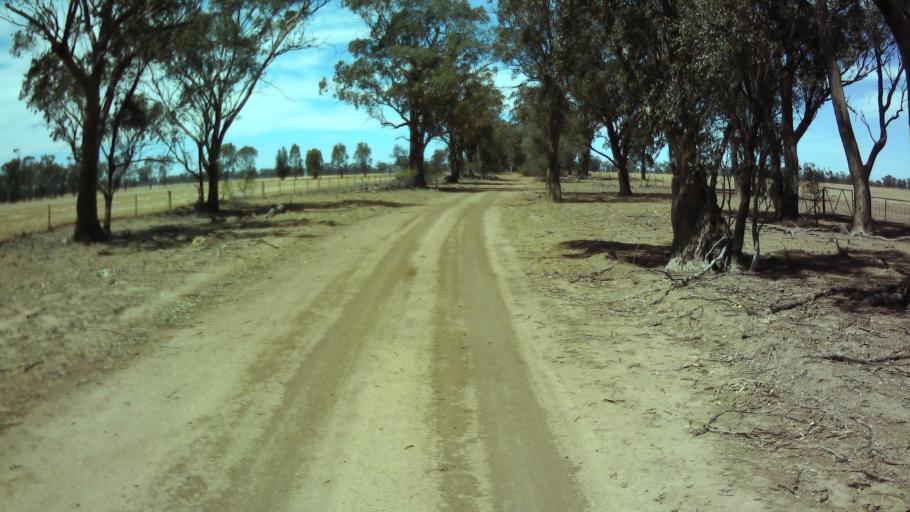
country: AU
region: New South Wales
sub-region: Weddin
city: Grenfell
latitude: -33.9206
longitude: 147.8047
